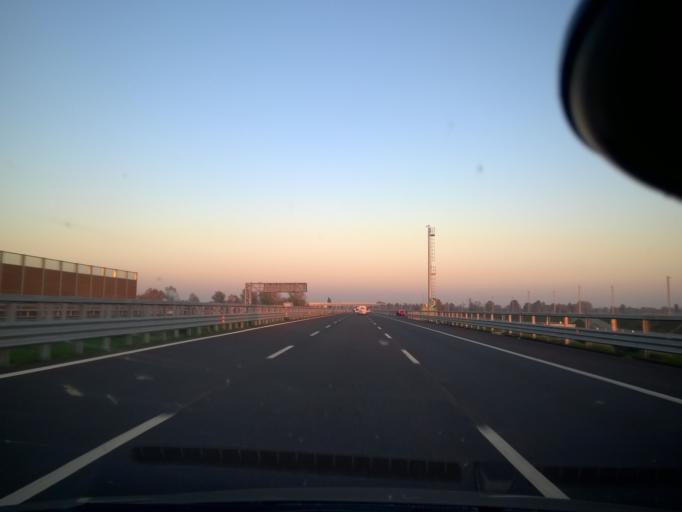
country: IT
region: Lombardy
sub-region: Provincia di Bergamo
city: Isso
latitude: 45.4880
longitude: 9.7587
